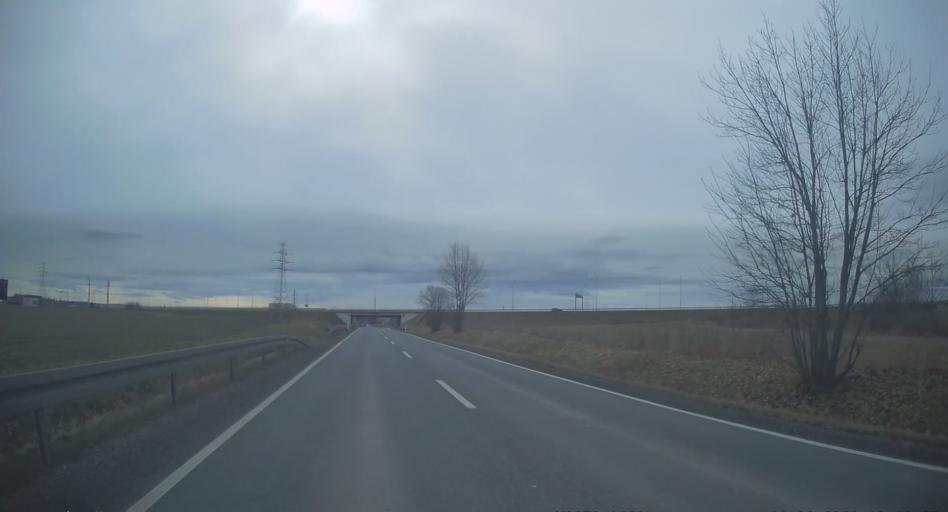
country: PL
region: Lesser Poland Voivodeship
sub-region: Powiat wielicki
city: Szarow
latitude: 49.9926
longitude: 20.2796
